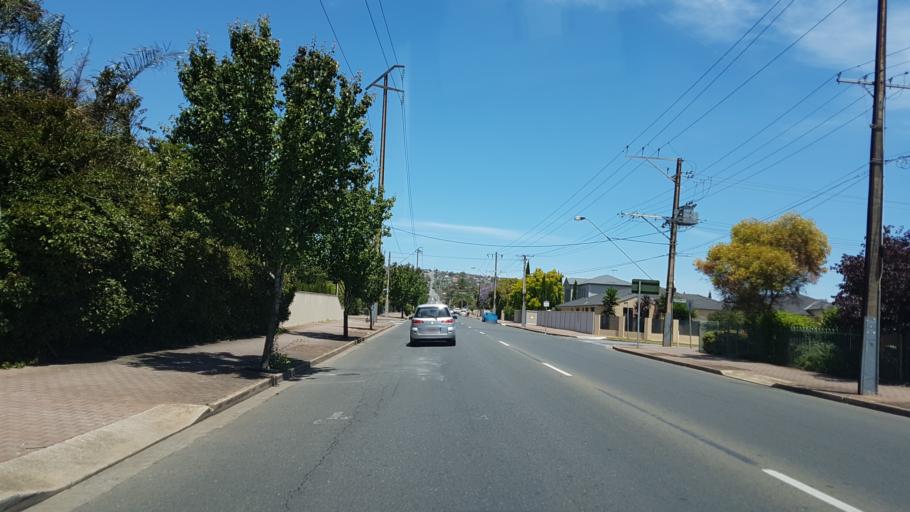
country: AU
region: South Australia
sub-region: Marion
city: Sturt
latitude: -35.0200
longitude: 138.5412
